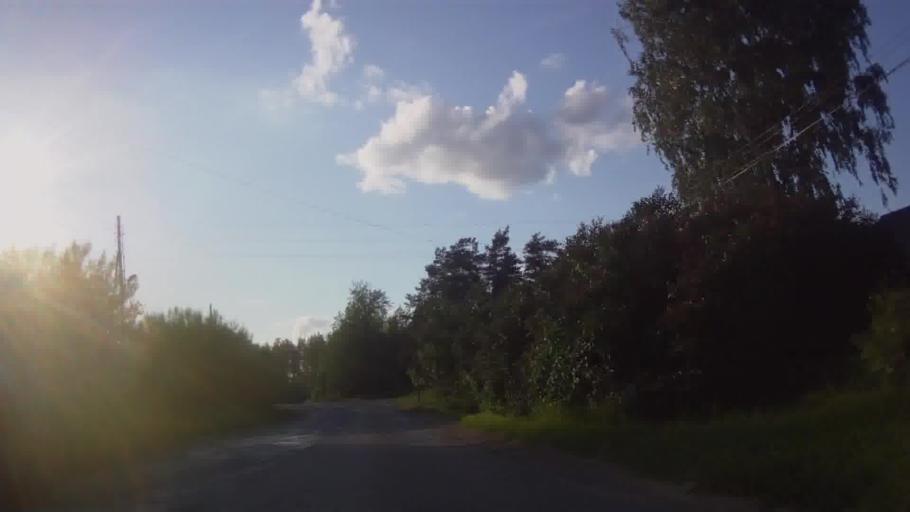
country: LV
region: Rezekne
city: Rezekne
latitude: 56.5305
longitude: 27.3152
